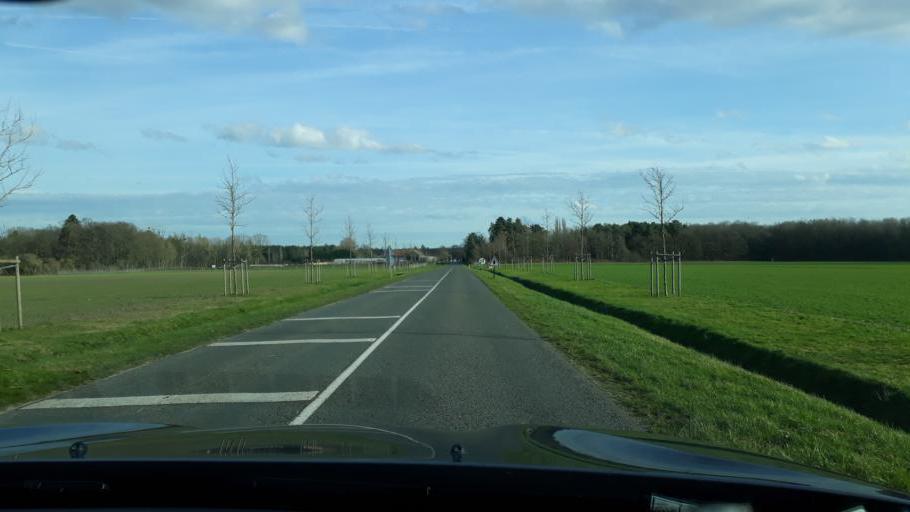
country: FR
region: Centre
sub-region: Departement du Loiret
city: Chilleurs-aux-Bois
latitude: 48.0592
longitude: 2.1686
